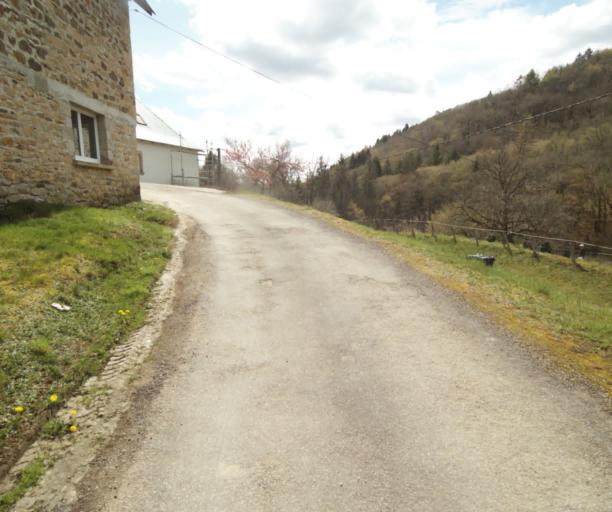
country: FR
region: Limousin
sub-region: Departement de la Correze
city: Sainte-Fortunade
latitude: 45.1858
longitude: 1.8761
